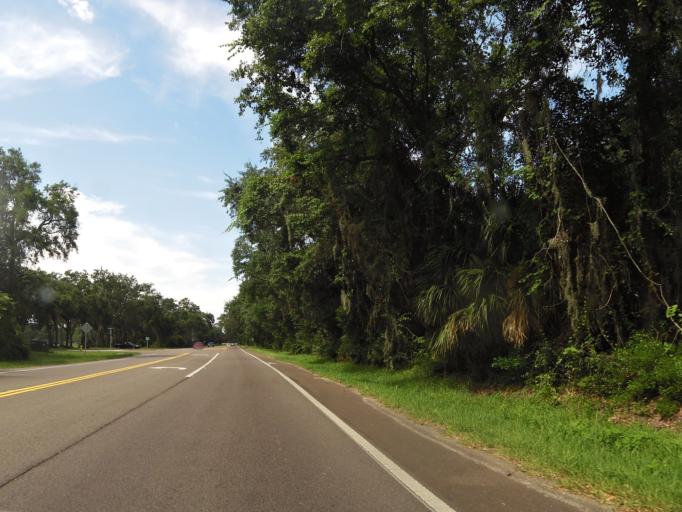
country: US
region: Florida
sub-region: Nassau County
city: Fernandina Beach
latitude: 30.6094
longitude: -81.4523
